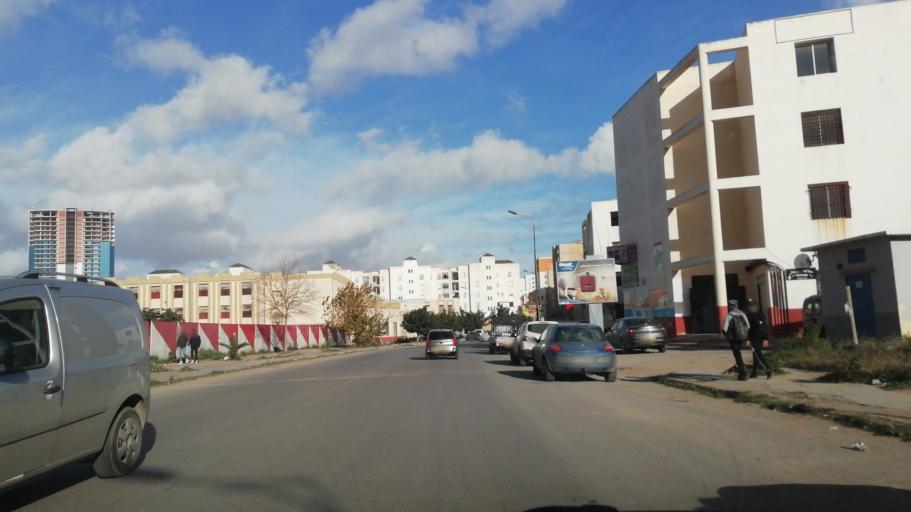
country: DZ
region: Oran
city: Bir el Djir
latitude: 35.7243
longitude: -0.5914
